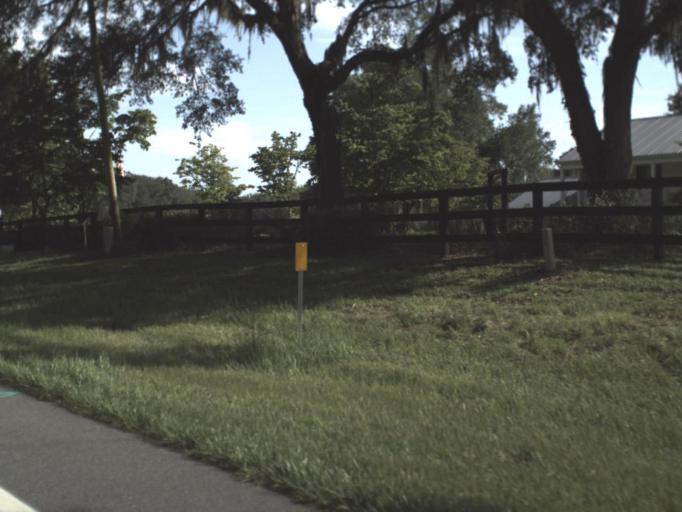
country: US
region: Florida
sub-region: Madison County
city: Madison
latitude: 30.4258
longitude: -83.3830
